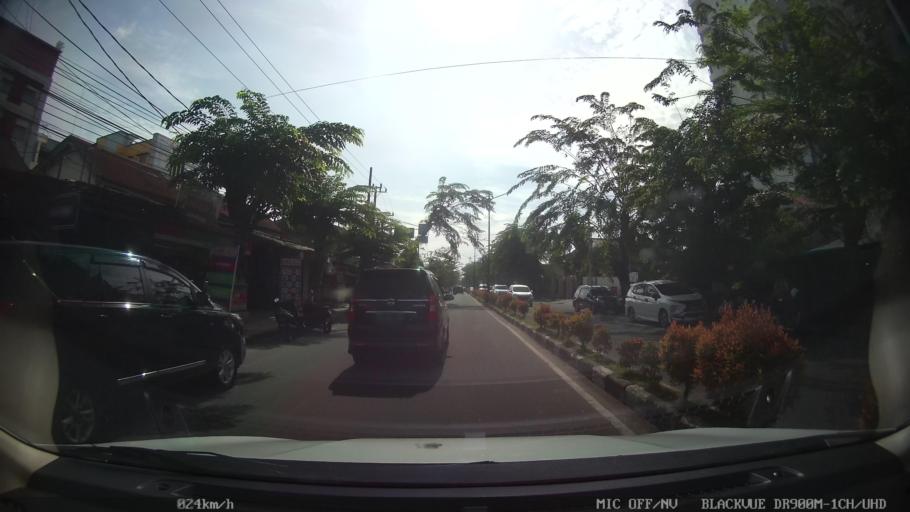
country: ID
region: North Sumatra
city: Medan
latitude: 3.5677
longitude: 98.6431
